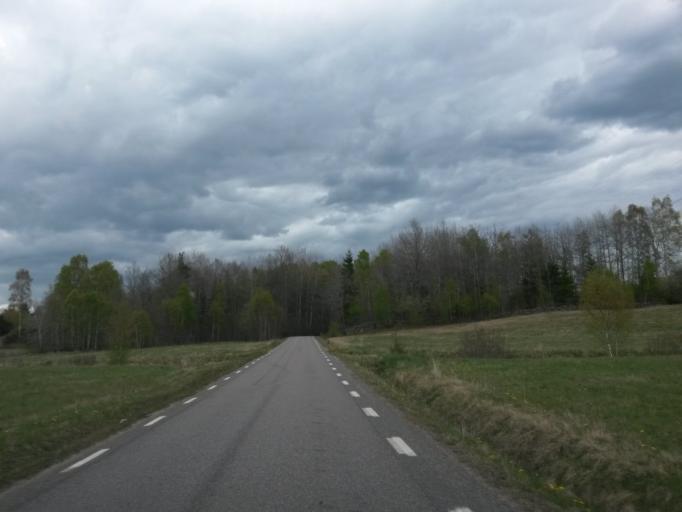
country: SE
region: Vaestra Goetaland
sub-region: Herrljunga Kommun
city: Herrljunga
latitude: 58.1408
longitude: 13.0425
